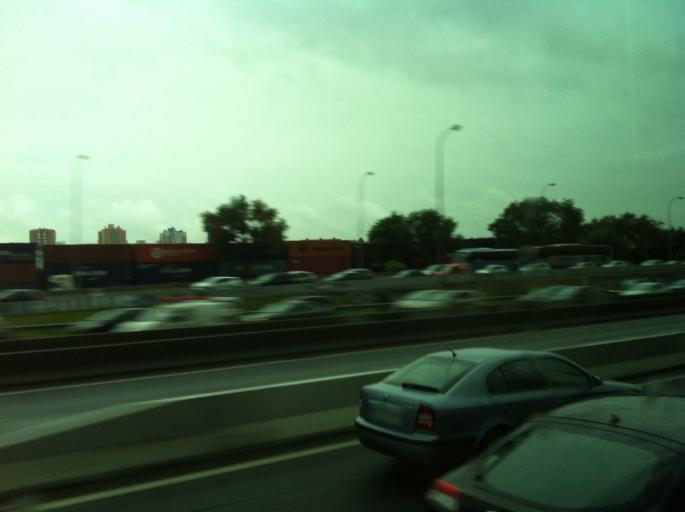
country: ES
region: Madrid
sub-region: Provincia de Madrid
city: Puente de Vallecas
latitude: 40.3895
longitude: -3.6798
